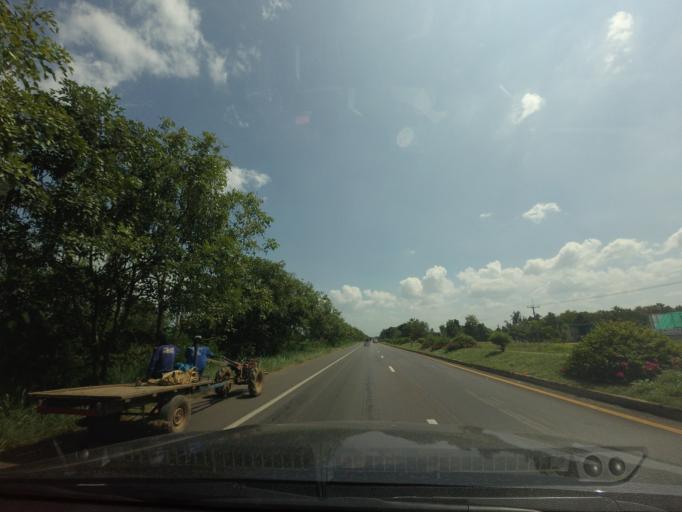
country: TH
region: Phetchabun
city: Nong Phai
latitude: 16.1104
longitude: 101.0399
